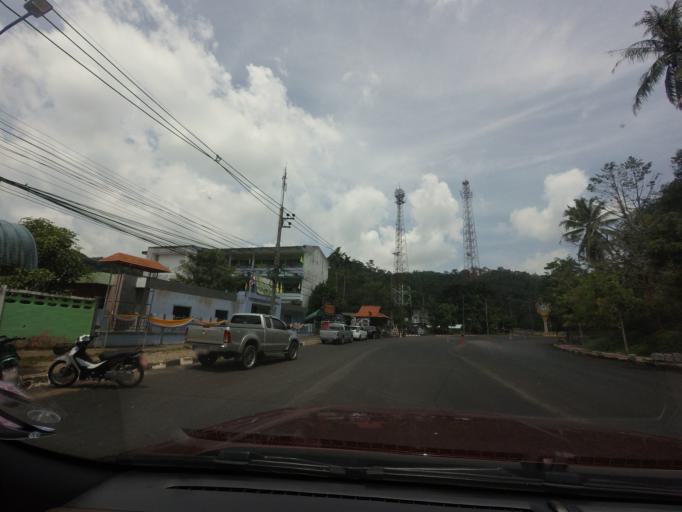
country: TH
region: Yala
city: Betong
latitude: 5.7486
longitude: 101.0365
